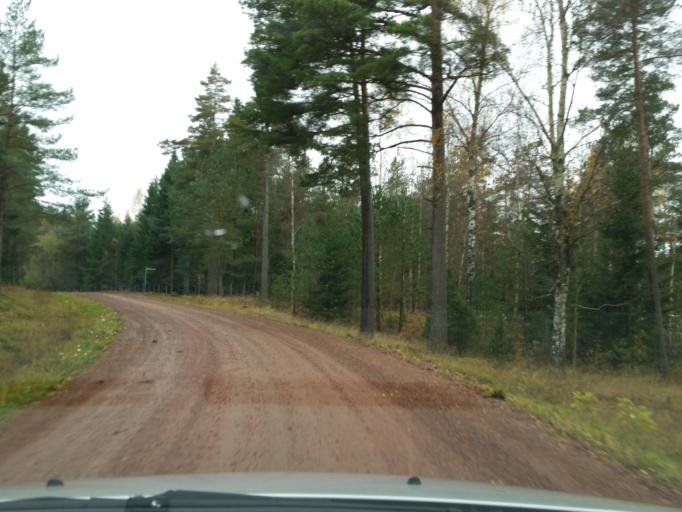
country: AX
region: Alands landsbygd
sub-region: Lumparland
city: Lumparland
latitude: 60.1111
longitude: 20.2626
